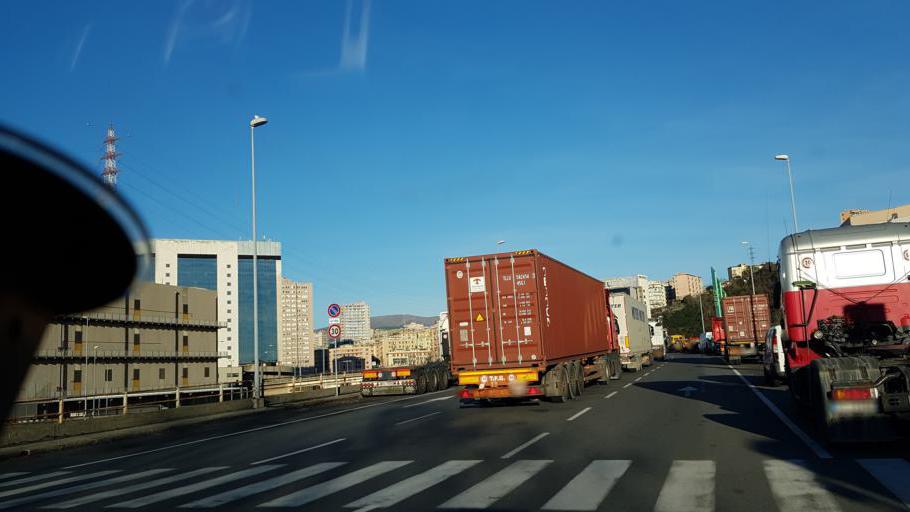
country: IT
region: Liguria
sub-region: Provincia di Genova
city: San Teodoro
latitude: 44.4075
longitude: 8.9049
